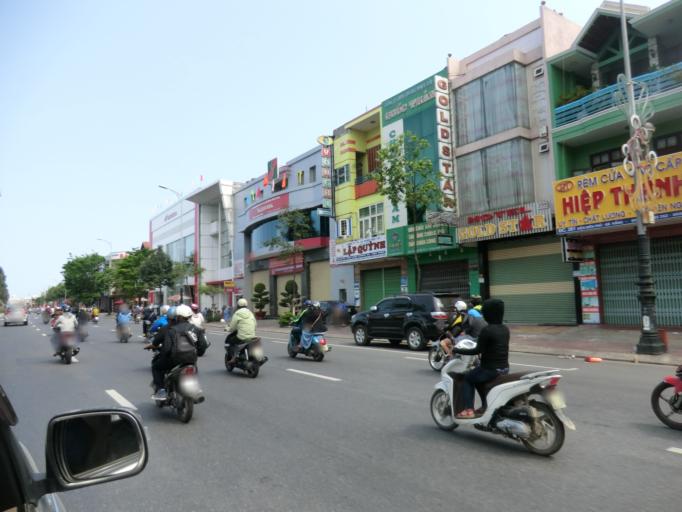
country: VN
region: Da Nang
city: Thanh Khe
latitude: 16.0657
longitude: 108.1941
